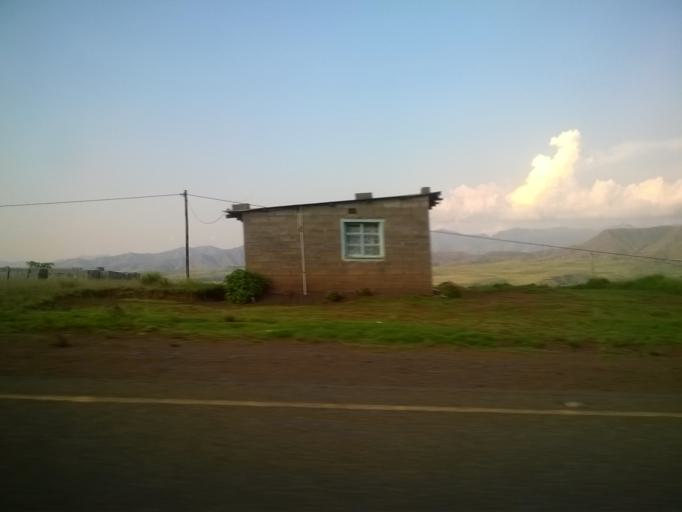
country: LS
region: Leribe
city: Leribe
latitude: -29.0244
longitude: 28.2270
